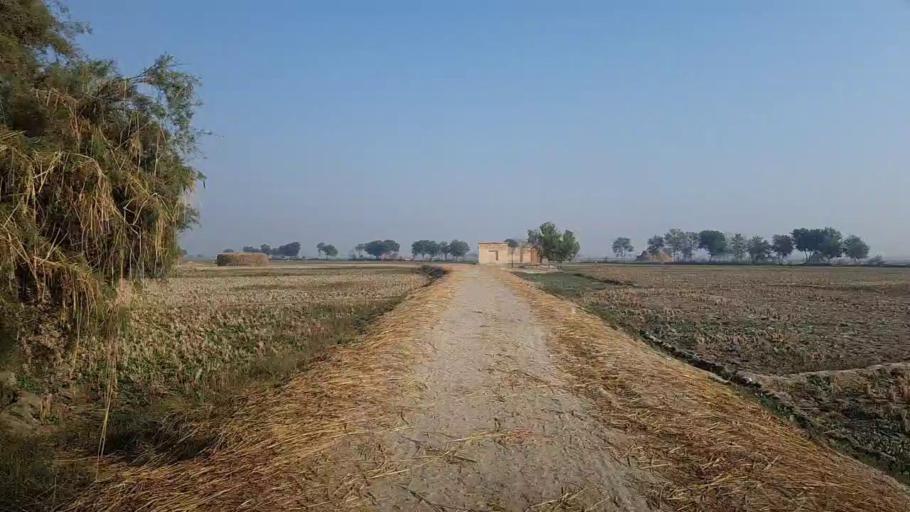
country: PK
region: Sindh
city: Radhan
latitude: 27.1188
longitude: 67.8963
